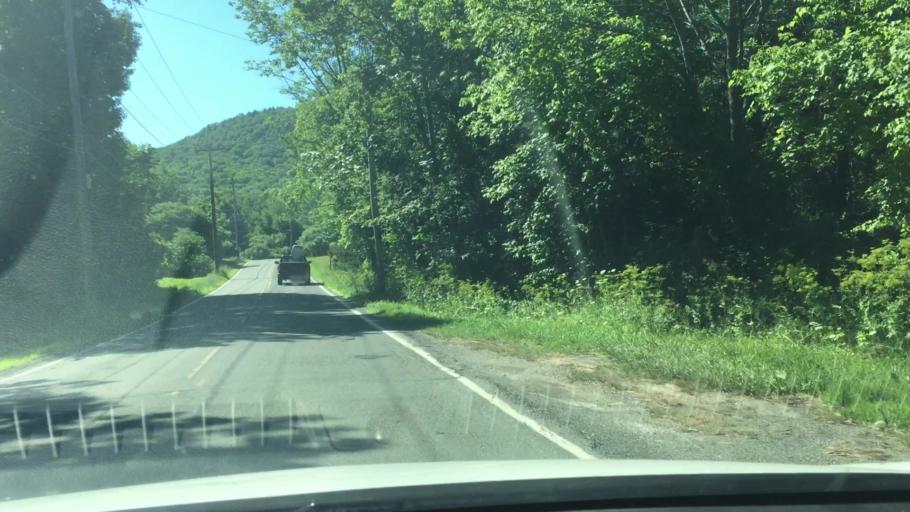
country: US
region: Massachusetts
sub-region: Berkshire County
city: Pittsfield
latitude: 42.4219
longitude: -73.2928
